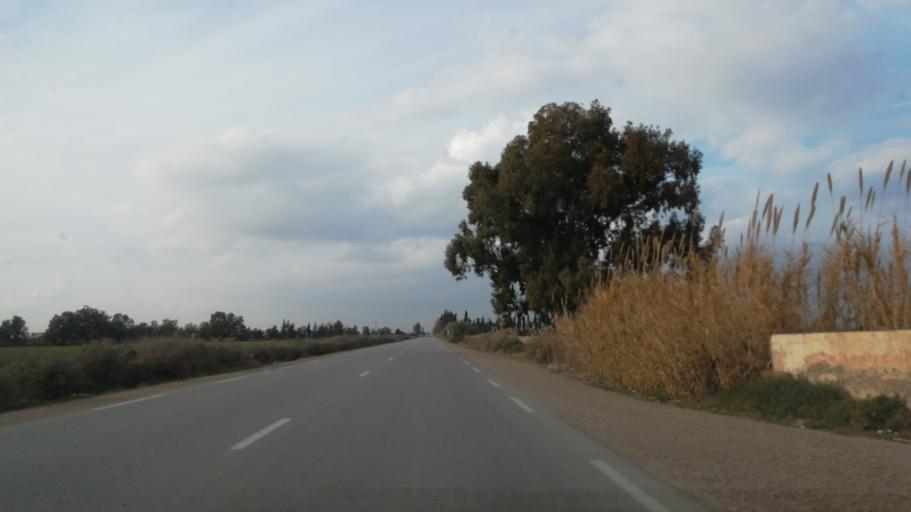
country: DZ
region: Mascara
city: Sig
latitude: 35.6751
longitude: -0.0062
